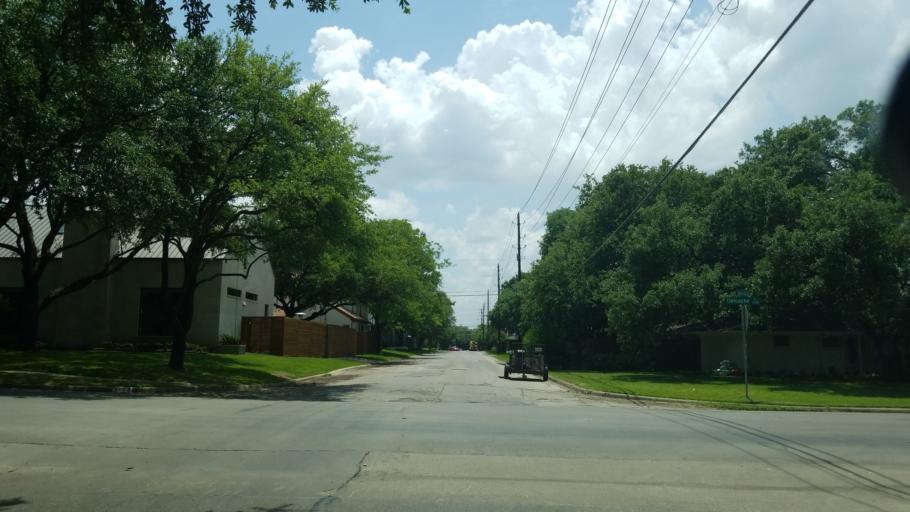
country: US
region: Texas
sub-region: Dallas County
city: University Park
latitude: 32.8707
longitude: -96.7915
